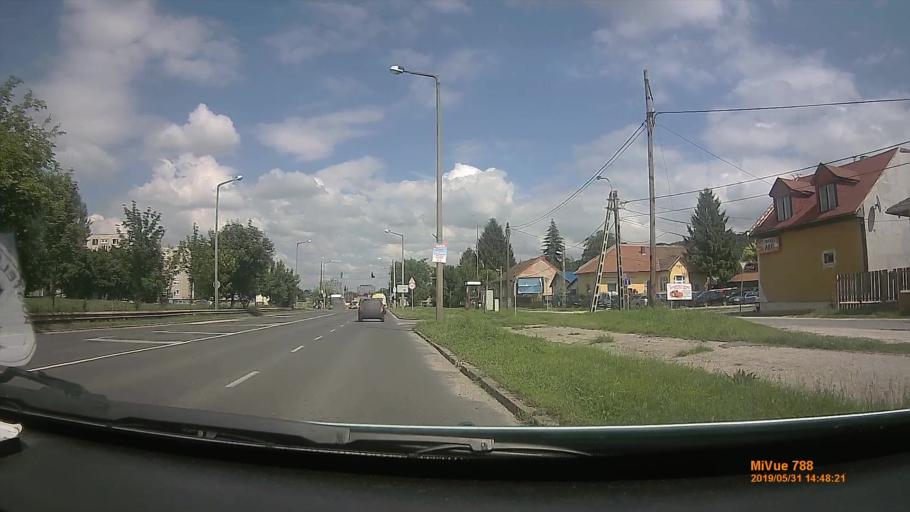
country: HU
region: Borsod-Abauj-Zemplen
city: Miskolc
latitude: 48.1013
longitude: 20.7564
